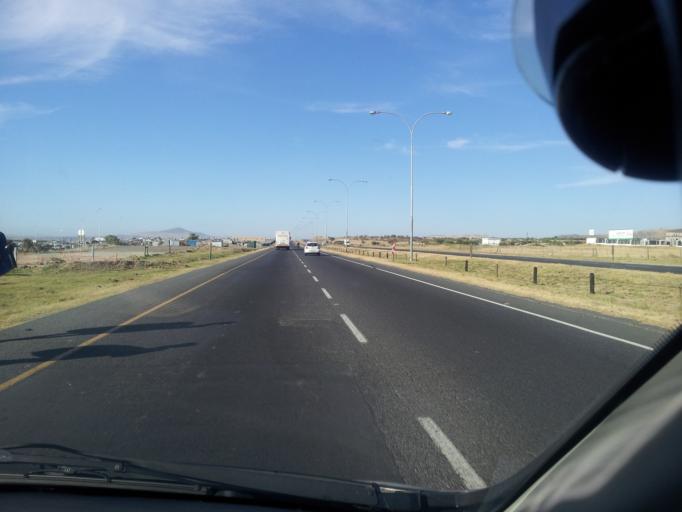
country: ZA
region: Western Cape
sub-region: City of Cape Town
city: Sunset Beach
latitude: -33.8299
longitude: 18.5396
